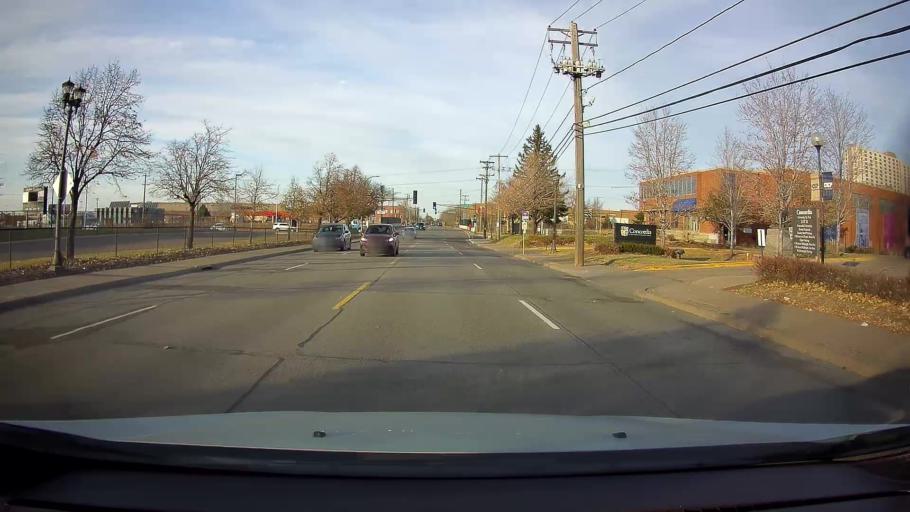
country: US
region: Minnesota
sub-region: Ramsey County
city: Falcon Heights
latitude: 44.9504
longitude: -93.1568
